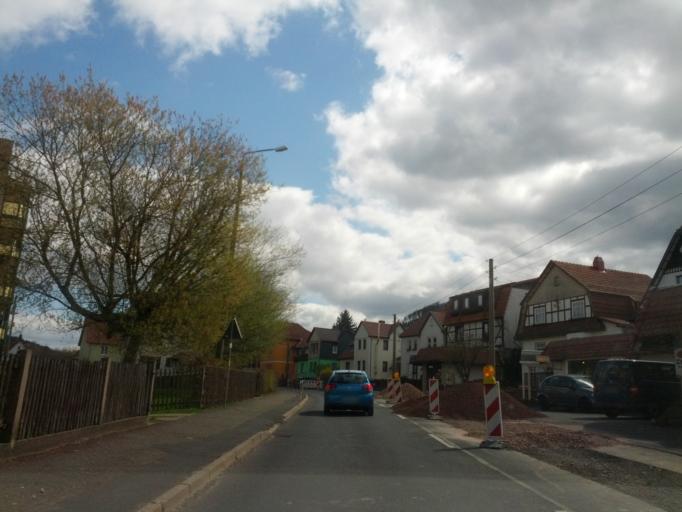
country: DE
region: Thuringia
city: Seebach
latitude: 50.9138
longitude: 10.4224
